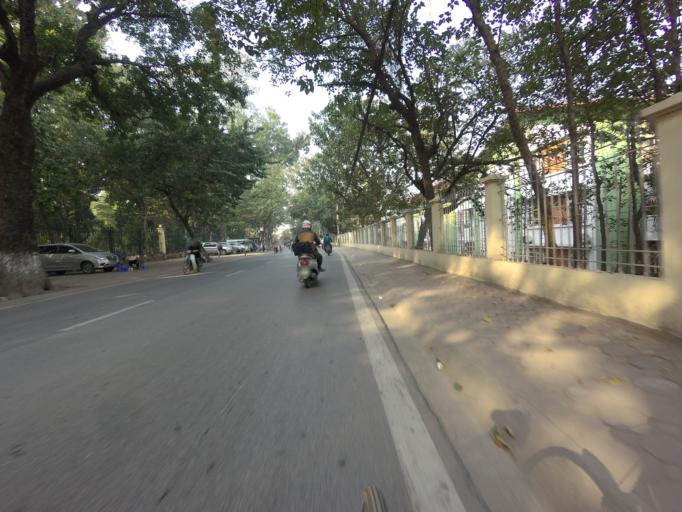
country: VN
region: Ha Noi
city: Hanoi
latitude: 21.0421
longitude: 105.8315
